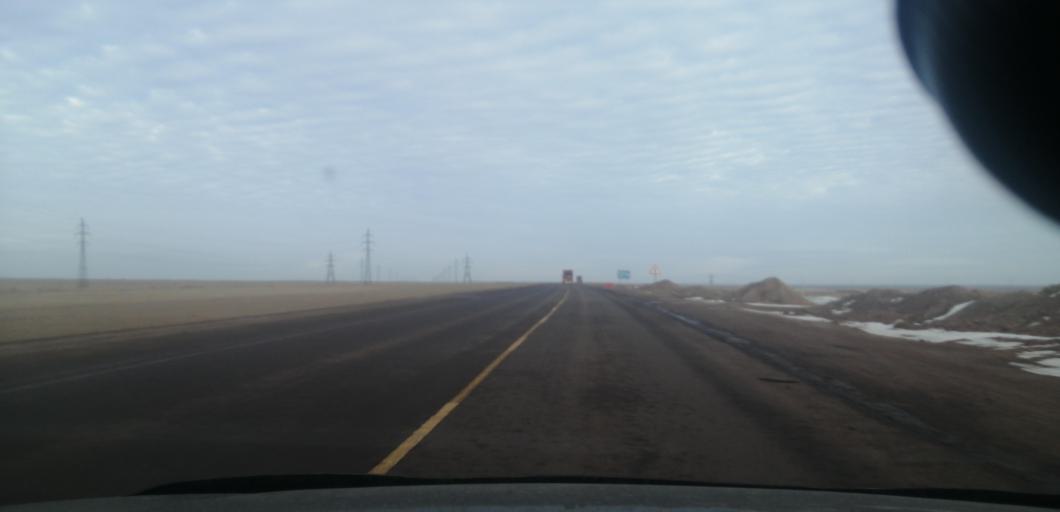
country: KZ
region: Qaraghandy
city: Balqash
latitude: 46.8041
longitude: 74.6981
